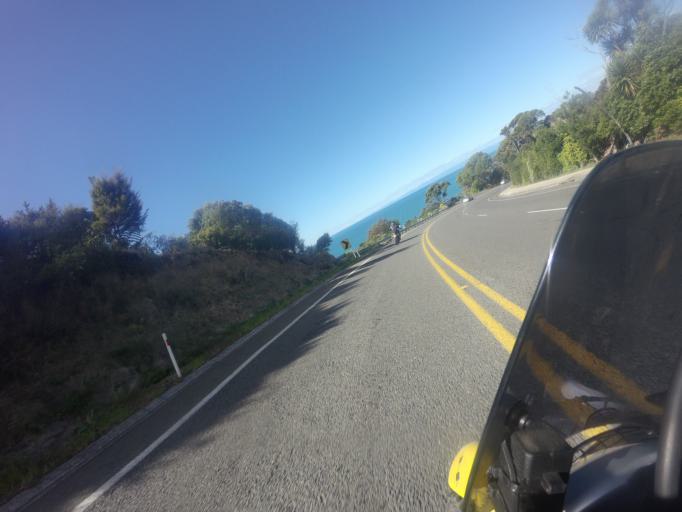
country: NZ
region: Bay of Plenty
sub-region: Whakatane District
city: Whakatane
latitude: -37.9615
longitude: 177.0245
